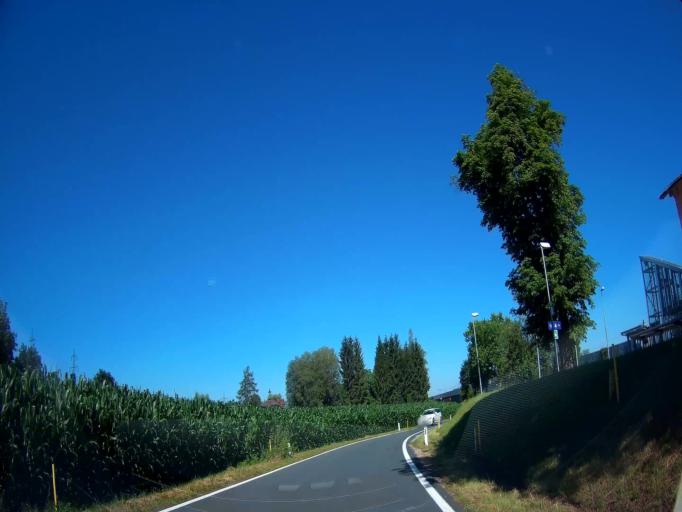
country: AT
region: Carinthia
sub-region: Politischer Bezirk Klagenfurt Land
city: Grafenstein
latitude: 46.6186
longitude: 14.4594
